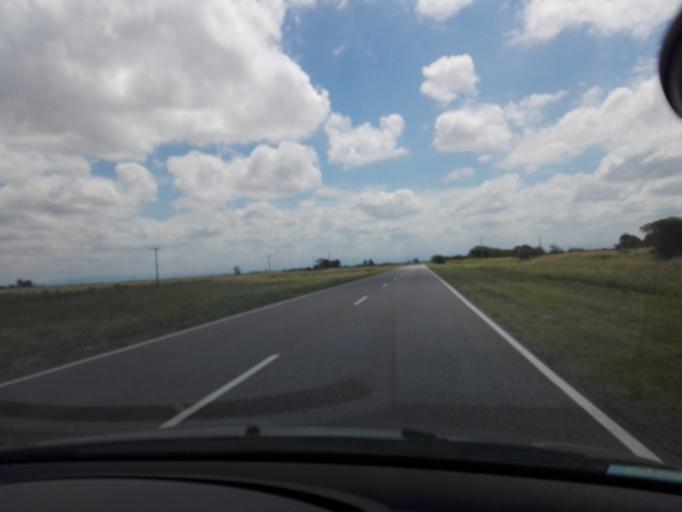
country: AR
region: Cordoba
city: Toledo
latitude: -31.6464
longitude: -64.0479
